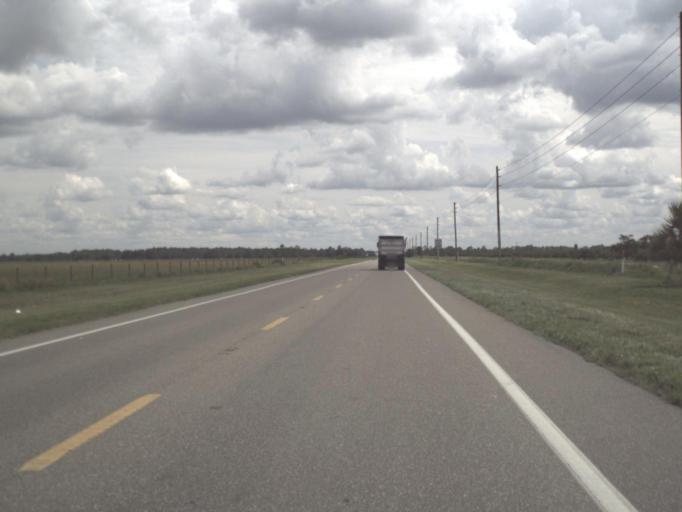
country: US
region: Florida
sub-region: DeSoto County
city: Nocatee
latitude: 27.0327
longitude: -81.7709
